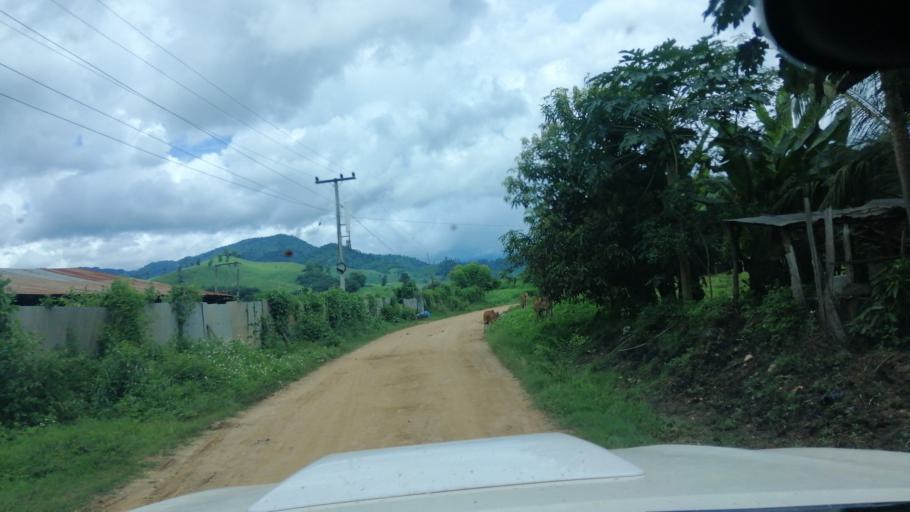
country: TH
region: Phayao
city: Phu Sang
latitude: 19.6958
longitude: 100.4975
